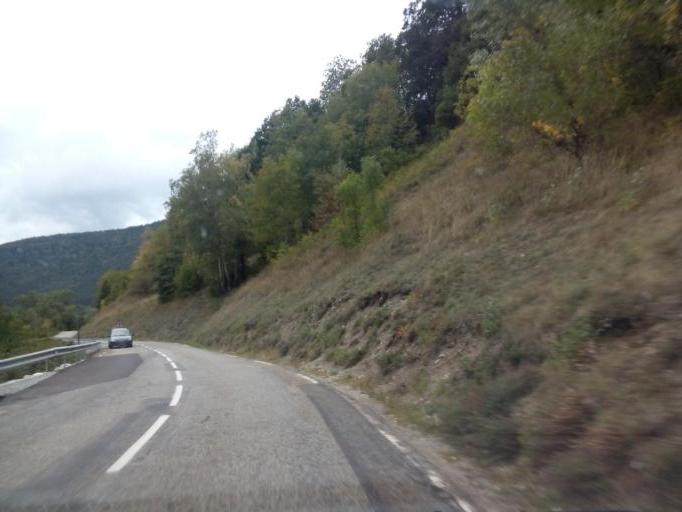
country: FR
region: Rhone-Alpes
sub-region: Departement de l'Isere
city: Pierre-Chatel
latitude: 44.9440
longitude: 5.8628
